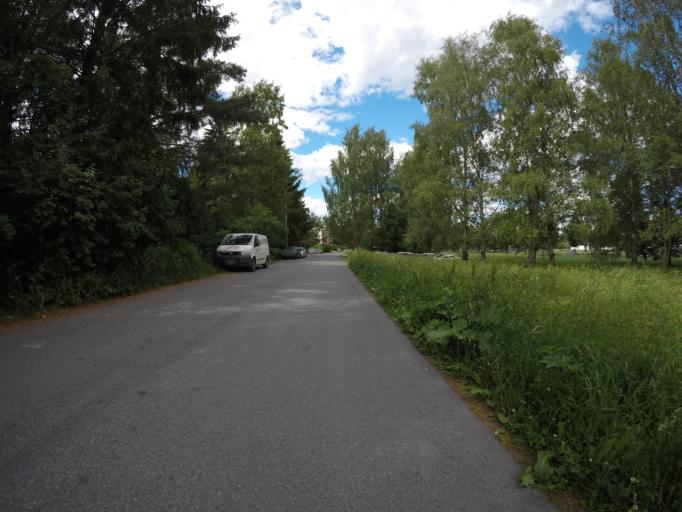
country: FI
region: Haeme
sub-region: Haemeenlinna
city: Haemeenlinna
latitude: 61.0010
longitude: 24.4269
